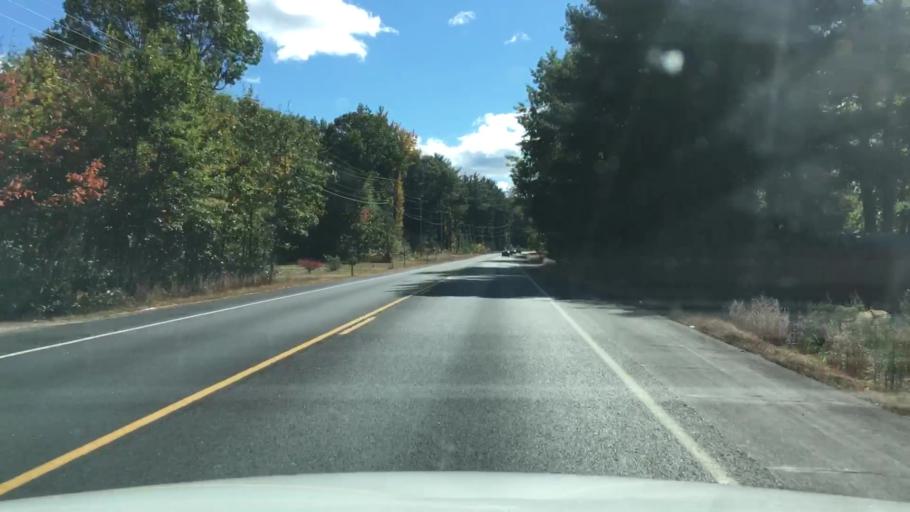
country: US
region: Maine
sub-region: York County
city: South Sanford
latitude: 43.4304
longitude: -70.7333
